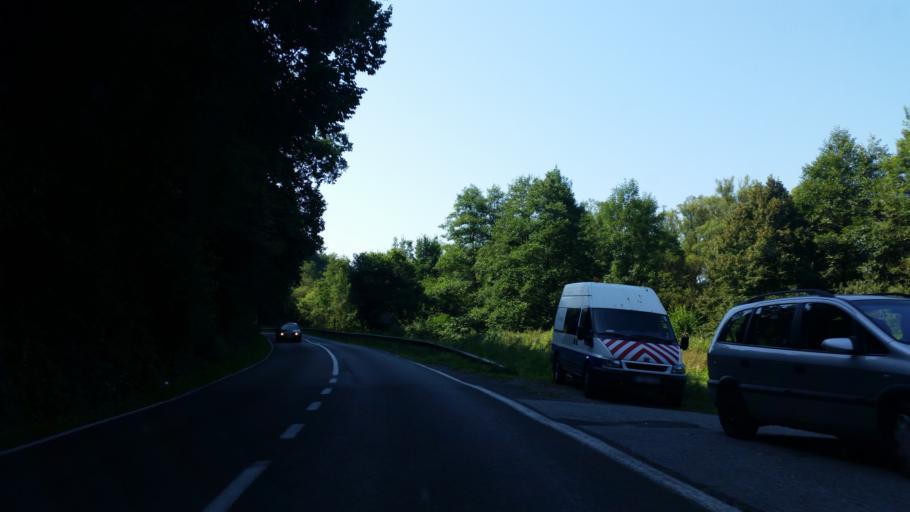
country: BE
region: Wallonia
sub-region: Province du Luxembourg
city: Durbuy
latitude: 50.3447
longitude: 5.4374
